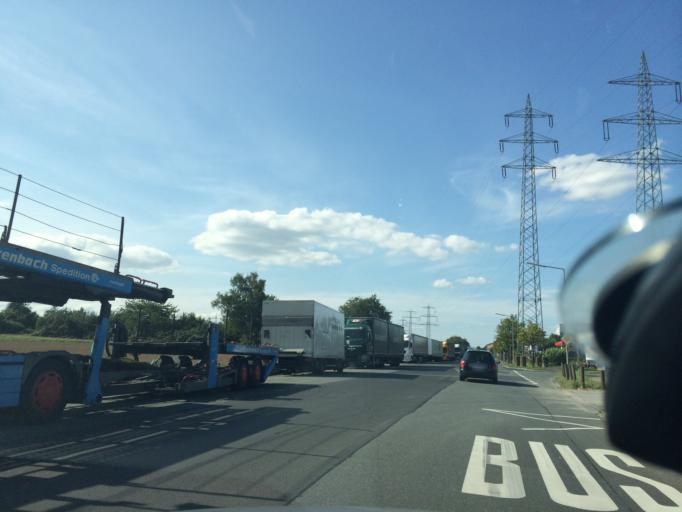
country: DE
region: Hesse
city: Morfelden-Walldorf
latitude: 49.9820
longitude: 8.5797
